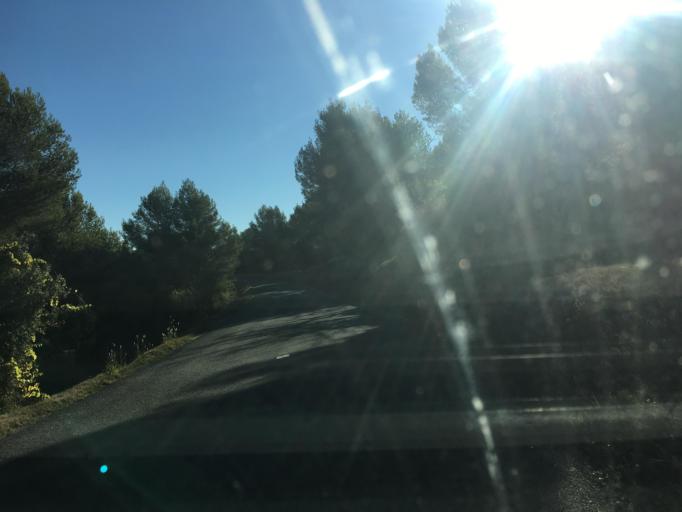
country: FR
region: Languedoc-Roussillon
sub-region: Departement de l'Aude
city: Fleury
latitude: 43.2352
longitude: 3.1755
